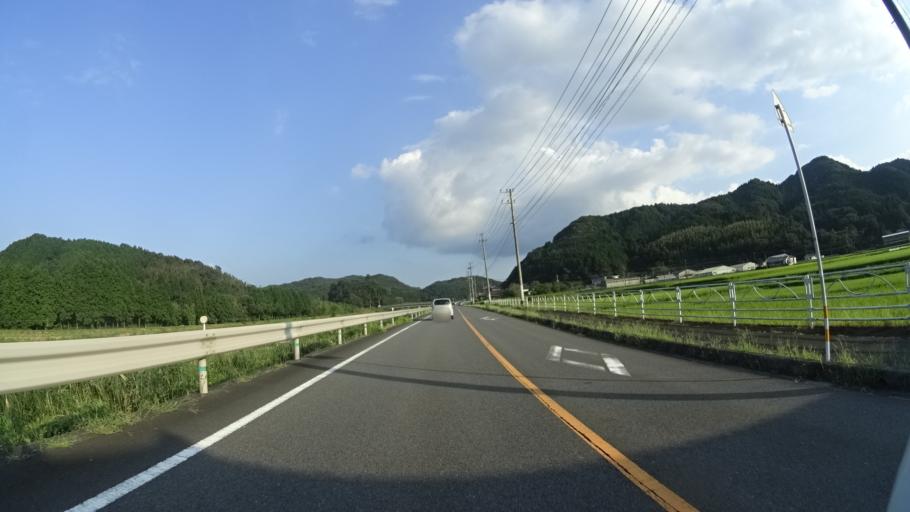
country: JP
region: Oita
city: Bungo-Takada-shi
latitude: 33.4344
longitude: 131.3696
